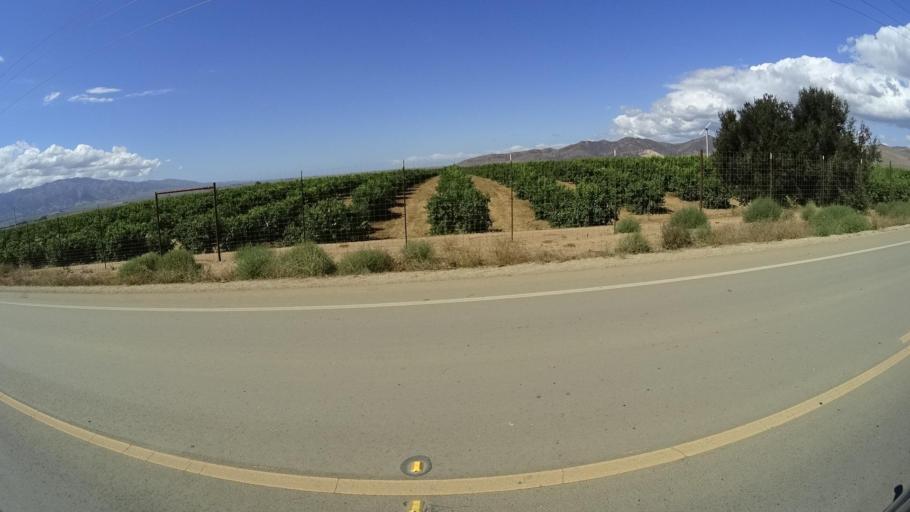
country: US
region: California
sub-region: Monterey County
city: Gonzales
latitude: 36.5306
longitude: -121.4115
